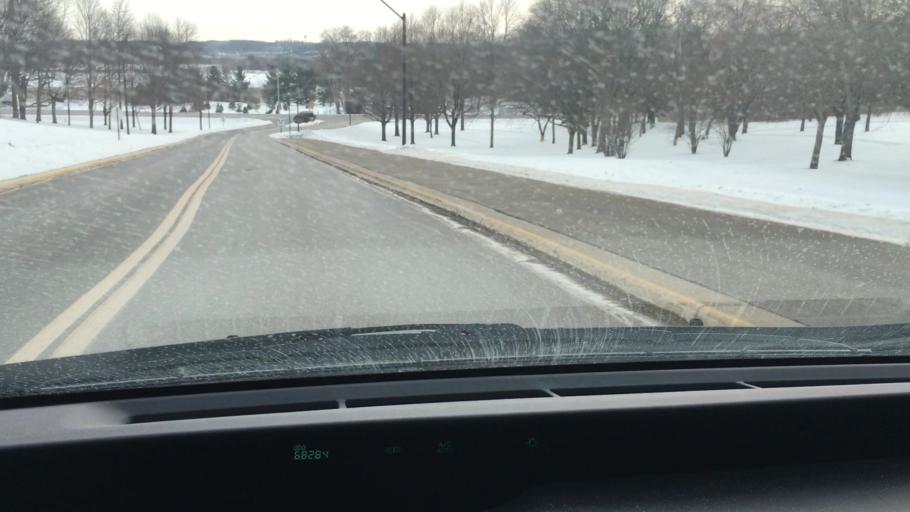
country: US
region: Minnesota
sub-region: Rice County
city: Northfield
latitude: 44.4586
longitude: -93.1878
